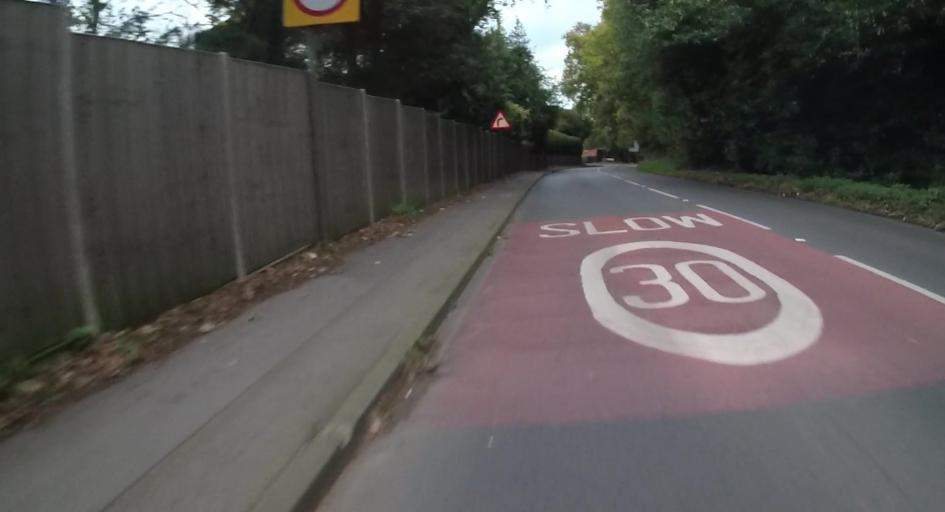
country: GB
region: England
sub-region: Wokingham
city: Finchampstead
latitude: 51.3630
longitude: -0.8570
